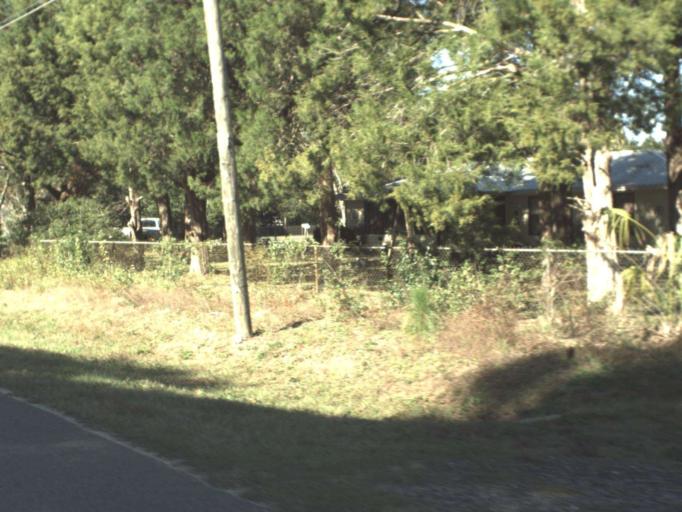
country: US
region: Florida
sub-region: Okaloosa County
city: Crestview
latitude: 30.7604
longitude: -86.6585
